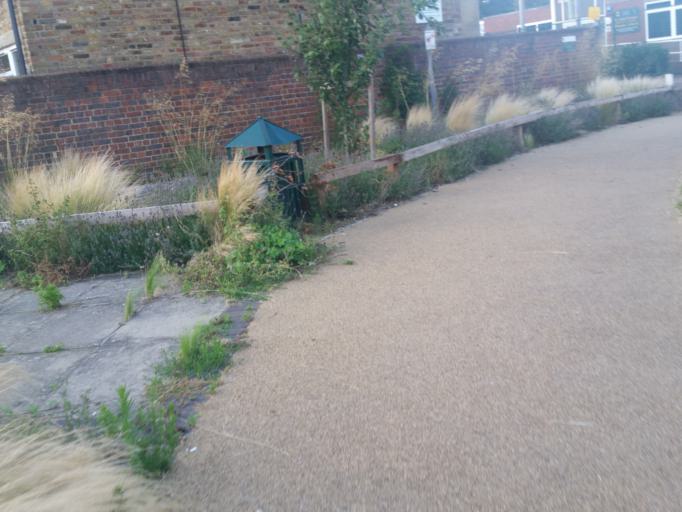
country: GB
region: England
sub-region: Greater London
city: Harringay
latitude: 51.5854
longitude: -0.0977
